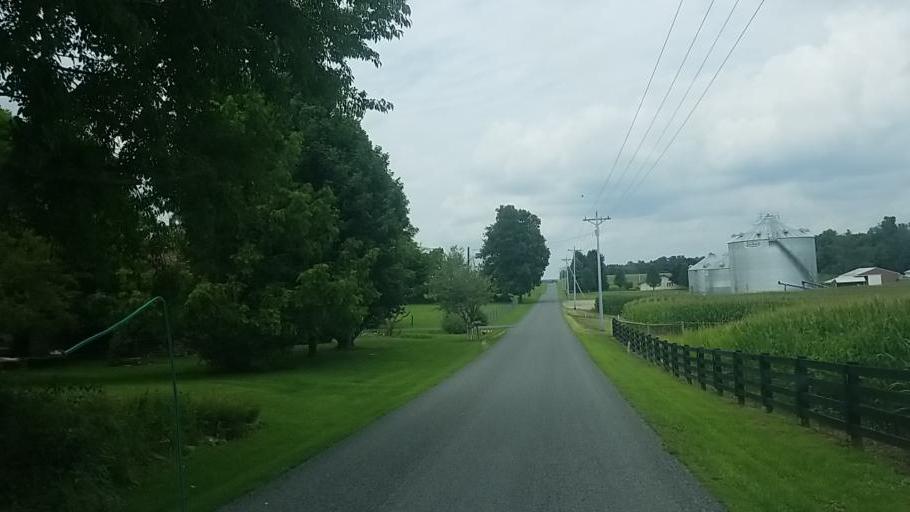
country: US
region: Ohio
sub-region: Licking County
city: Utica
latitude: 40.2314
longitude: -82.3920
